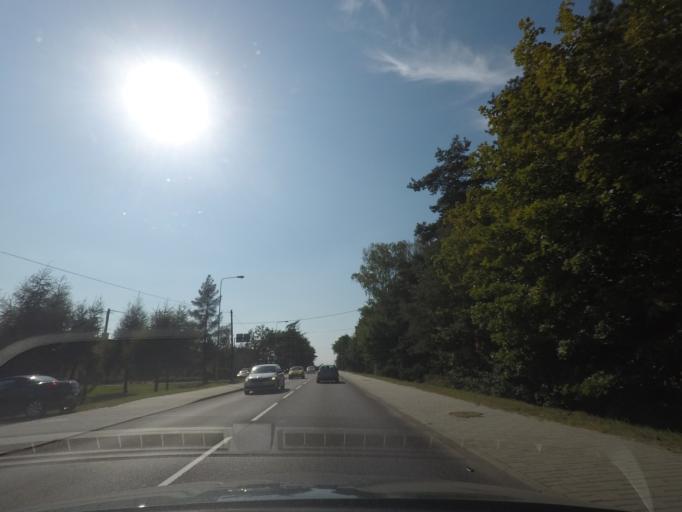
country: PL
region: Silesian Voivodeship
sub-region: Powiat pszczynski
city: Rudziczka
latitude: 50.0387
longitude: 18.7398
